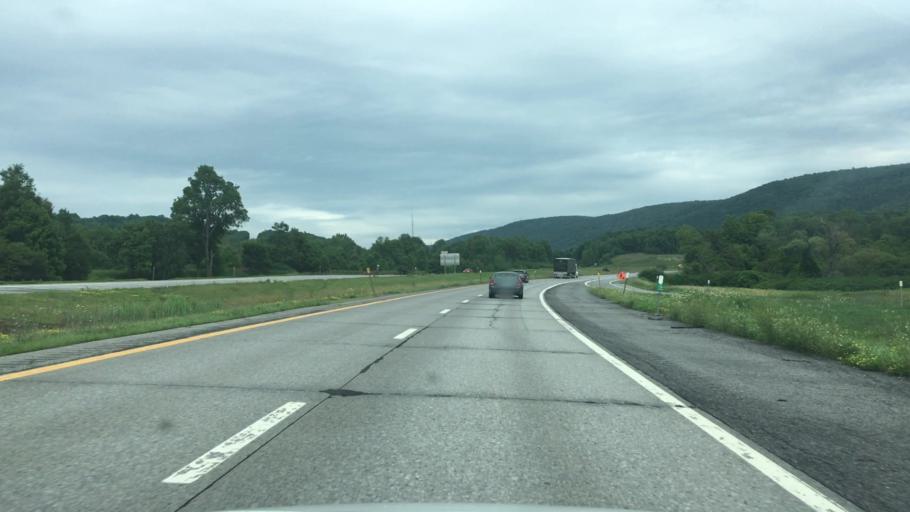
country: US
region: New York
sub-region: Otsego County
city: Worcester
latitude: 42.5936
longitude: -74.7246
